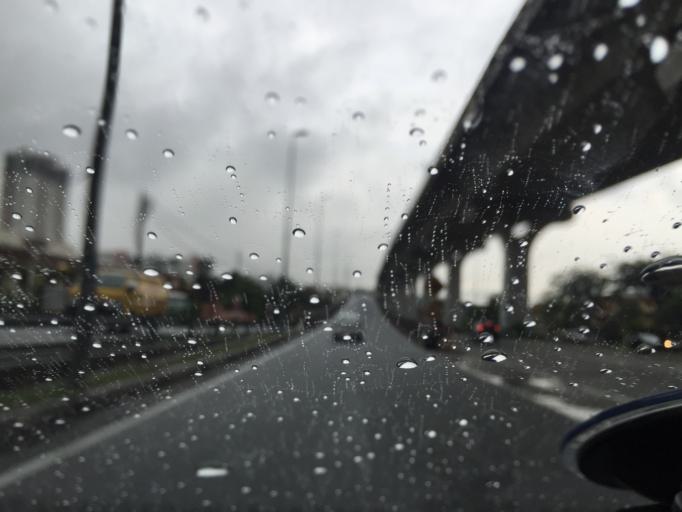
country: MY
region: Selangor
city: Subang Jaya
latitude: 3.0702
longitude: 101.5929
